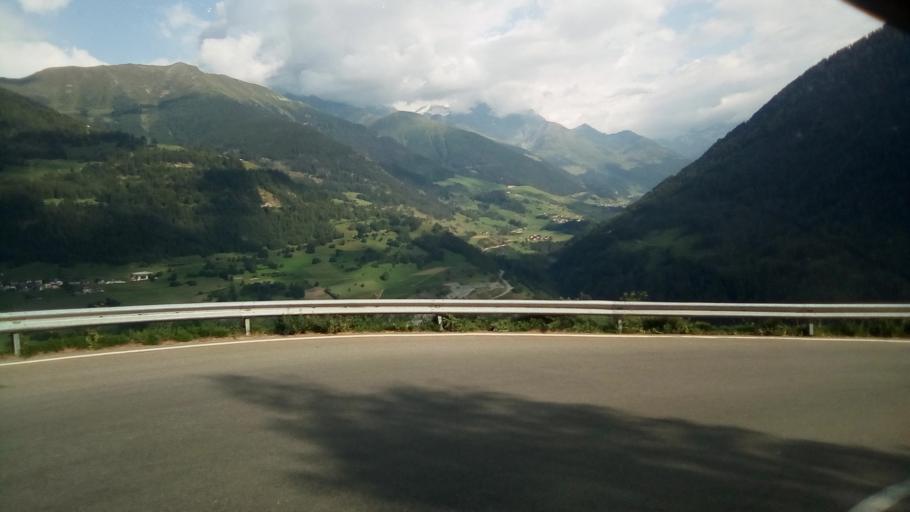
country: CH
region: Valais
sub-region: Entremont District
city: Orsieres
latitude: 46.0312
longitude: 7.1355
